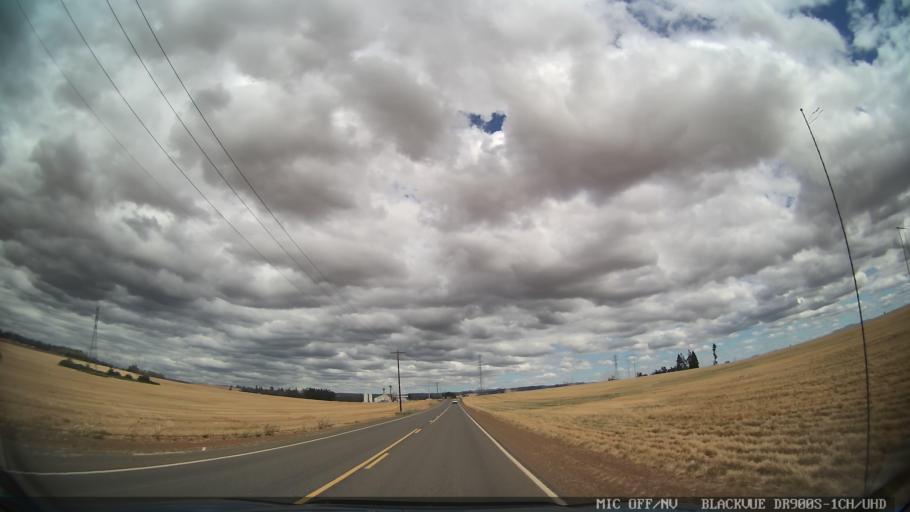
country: US
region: Oregon
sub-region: Marion County
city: Sublimity
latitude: 44.8663
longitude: -122.7969
